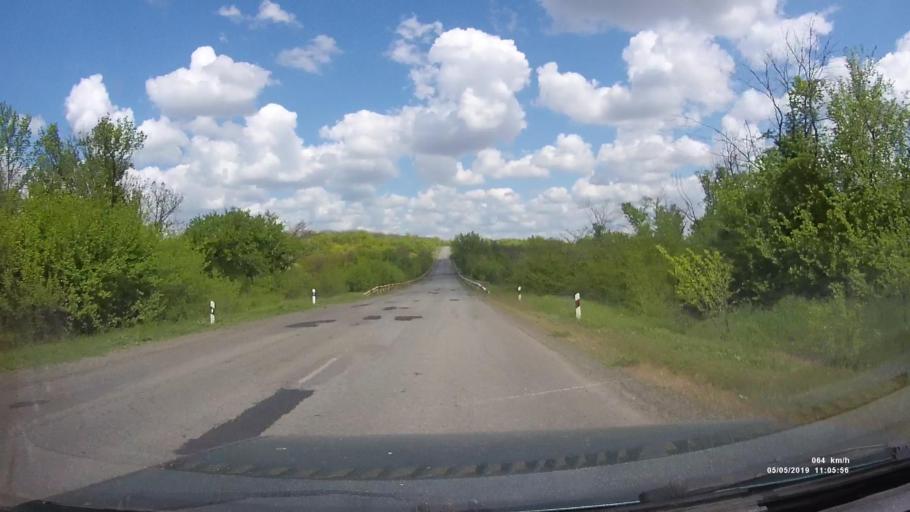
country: RU
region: Rostov
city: Ust'-Donetskiy
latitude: 47.7108
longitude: 40.9112
